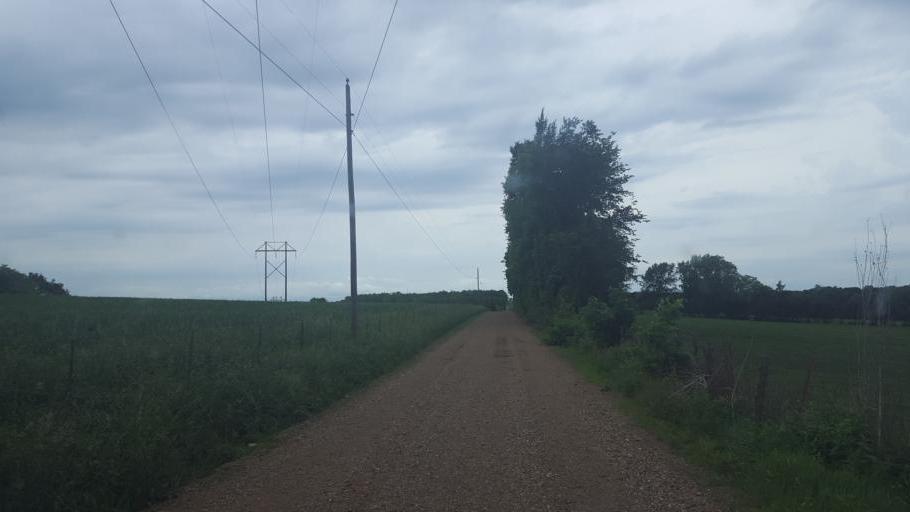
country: US
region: Missouri
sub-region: Moniteau County
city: California
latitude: 38.6810
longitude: -92.5983
